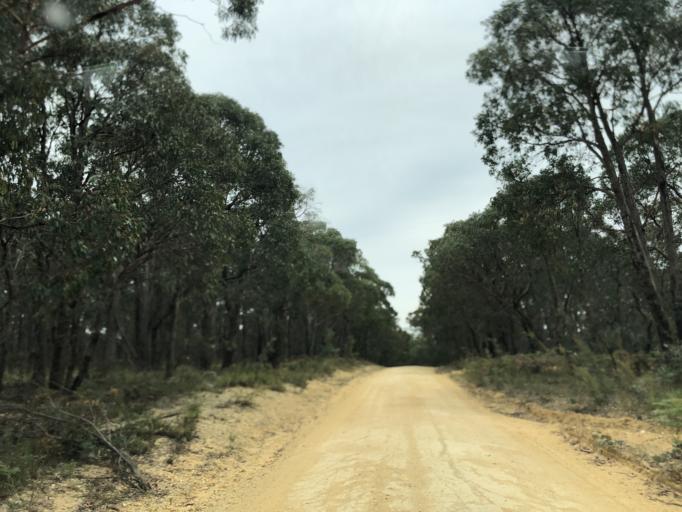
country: AU
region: Victoria
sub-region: Moorabool
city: Bacchus Marsh
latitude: -37.5011
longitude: 144.3449
